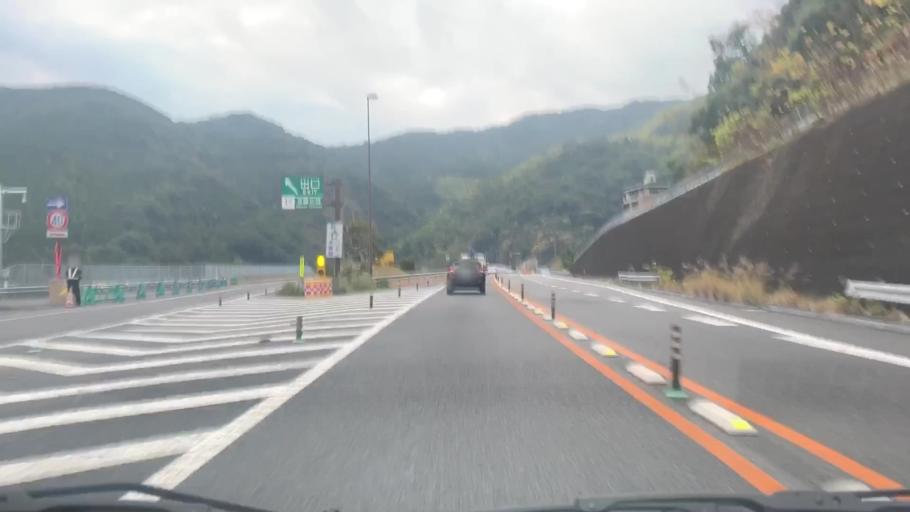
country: JP
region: Nagasaki
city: Nagasaki-shi
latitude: 32.7547
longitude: 129.9285
